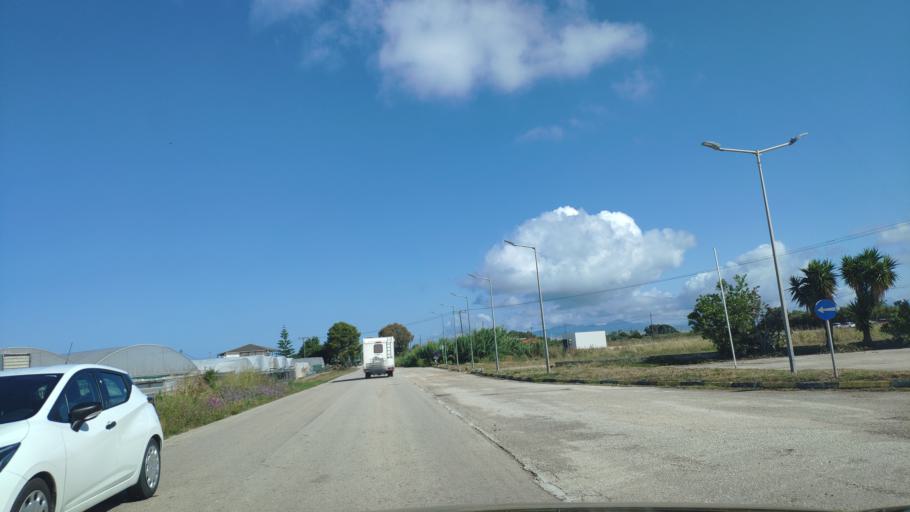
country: GR
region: Epirus
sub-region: Nomos Prevezis
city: Preveza
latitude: 38.9331
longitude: 20.7722
